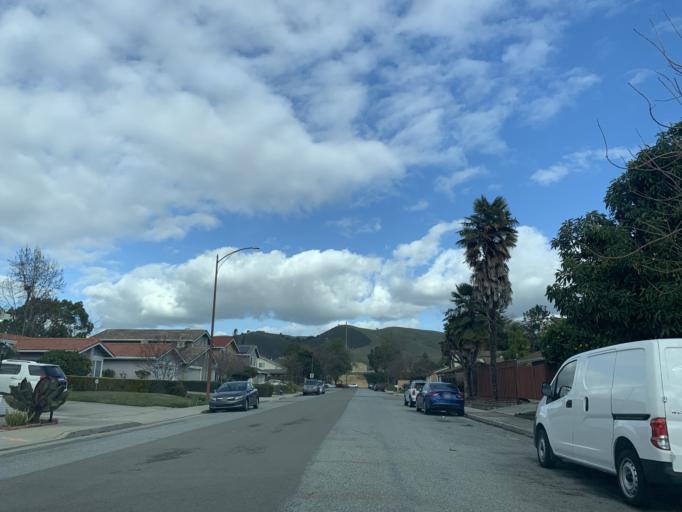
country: US
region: California
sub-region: Santa Clara County
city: Seven Trees
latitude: 37.2432
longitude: -121.7772
